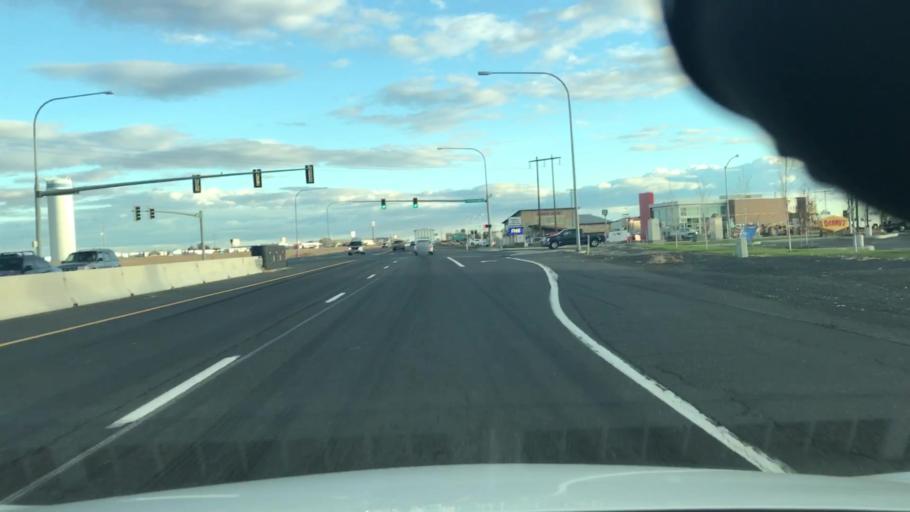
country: US
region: Washington
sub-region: Grant County
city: Moses Lake
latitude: 47.1067
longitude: -119.2527
